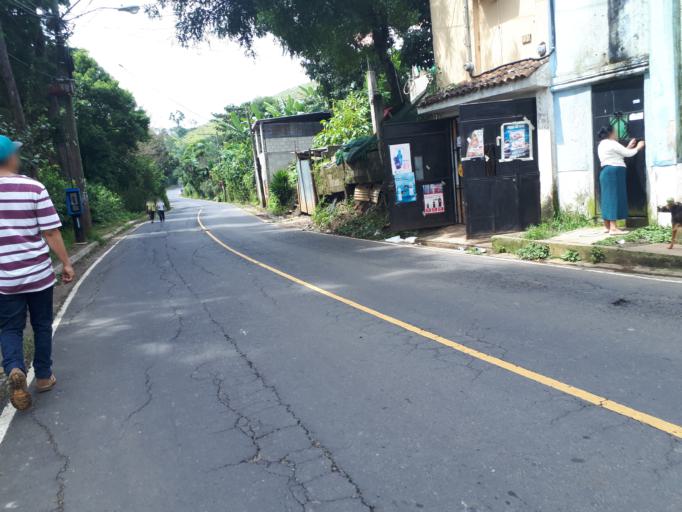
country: GT
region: Guatemala
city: Villa Canales
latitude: 14.4598
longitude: -90.5117
